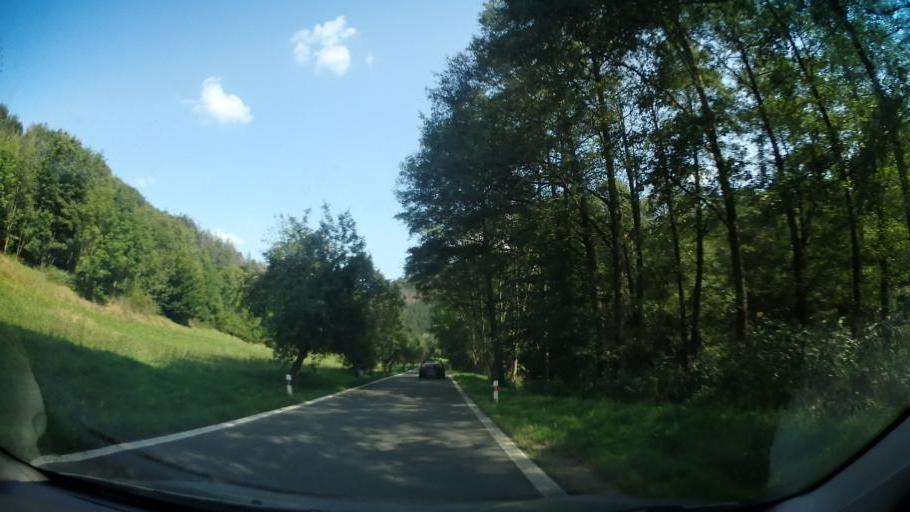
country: CZ
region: South Moravian
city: Olesnice
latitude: 49.5340
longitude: 16.3481
